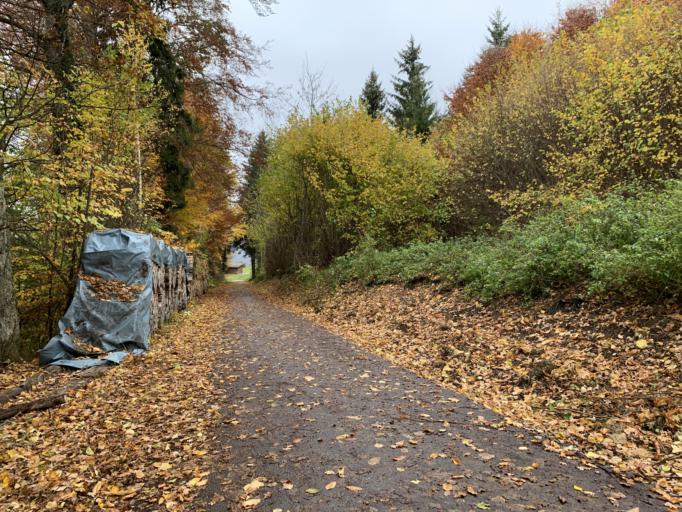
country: CH
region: Zurich
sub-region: Bezirk Pfaeffikon
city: Hittnau / Hittnau (Dorf)
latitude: 47.3600
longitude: 8.8471
